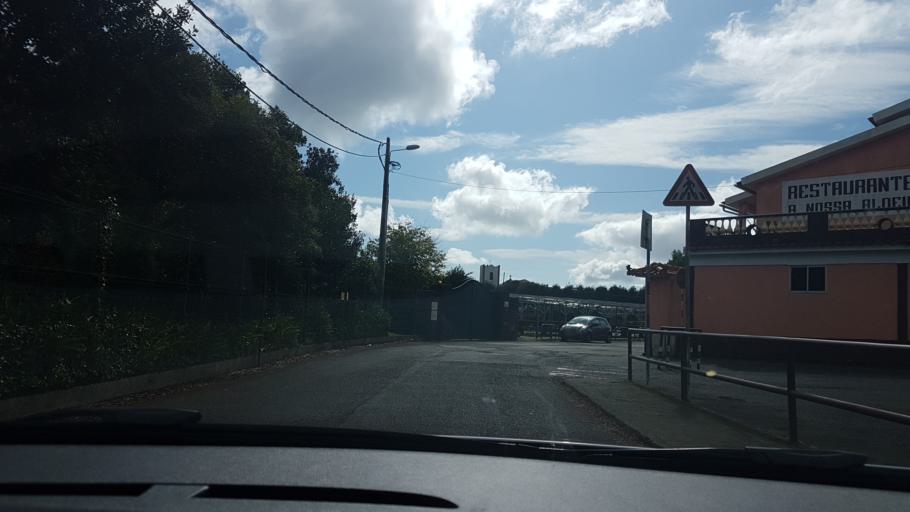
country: PT
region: Madeira
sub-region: Santa Cruz
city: Santa Cruz
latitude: 32.7264
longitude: -16.8205
